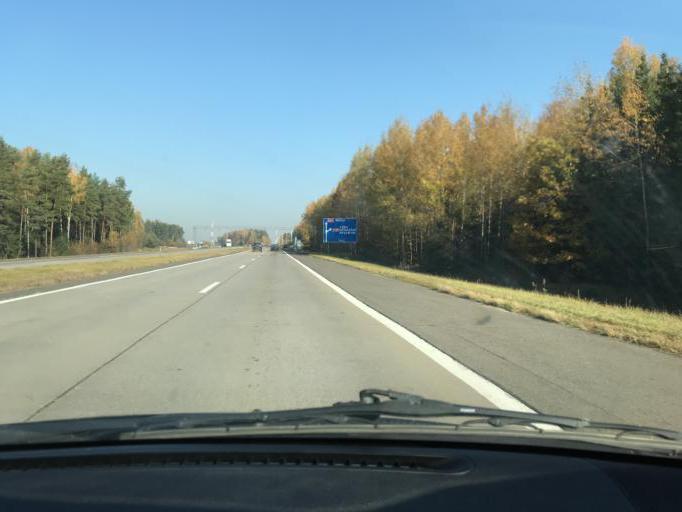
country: BY
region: Minsk
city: Uzda
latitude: 53.4177
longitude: 27.4890
